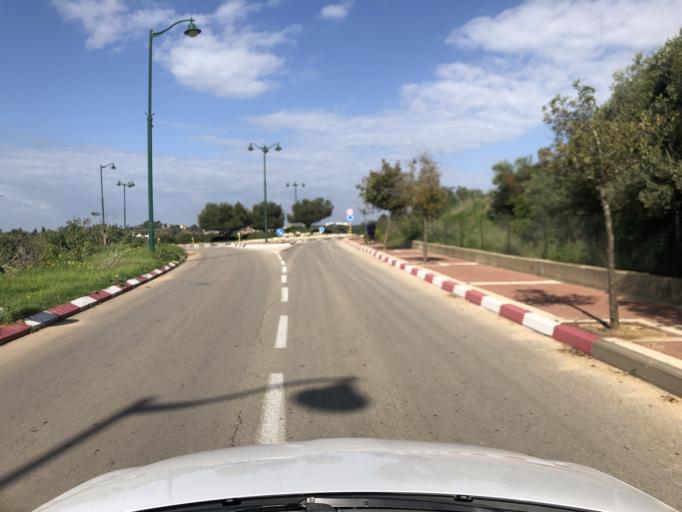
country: IL
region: Central District
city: Ness Ziona
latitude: 31.9144
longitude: 34.7829
